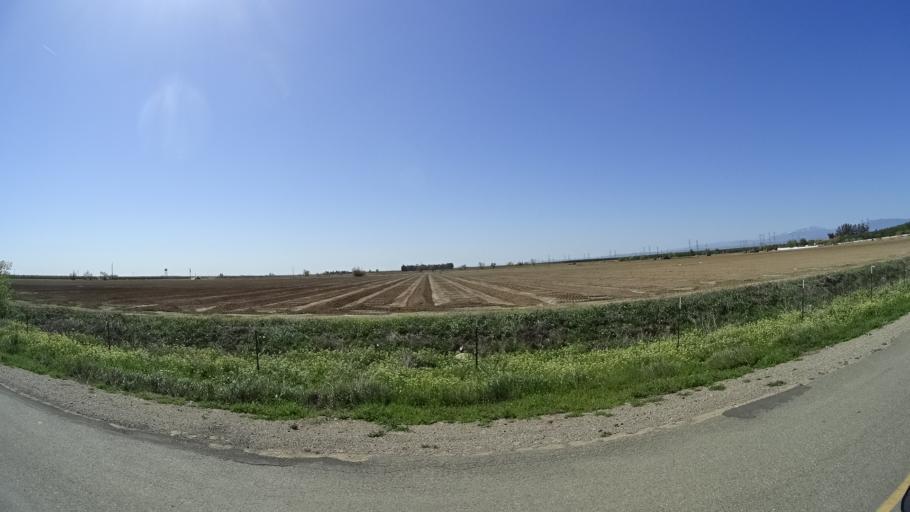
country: US
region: California
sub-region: Glenn County
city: Orland
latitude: 39.6974
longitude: -122.2576
